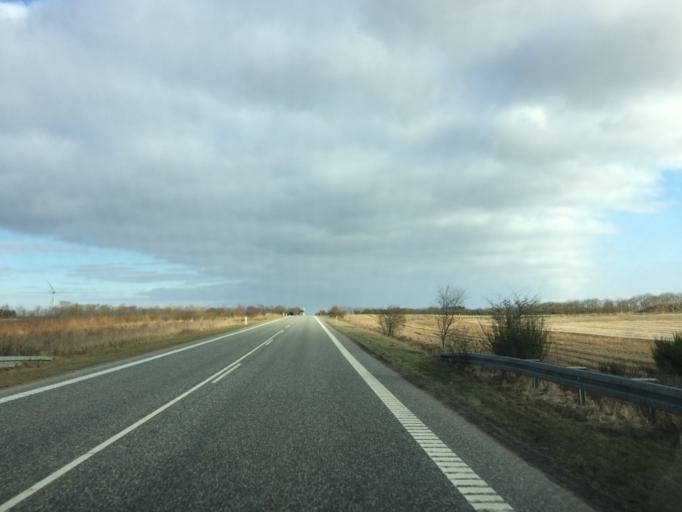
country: DK
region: Central Jutland
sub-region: Holstebro Kommune
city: Vinderup
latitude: 56.3761
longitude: 8.7543
